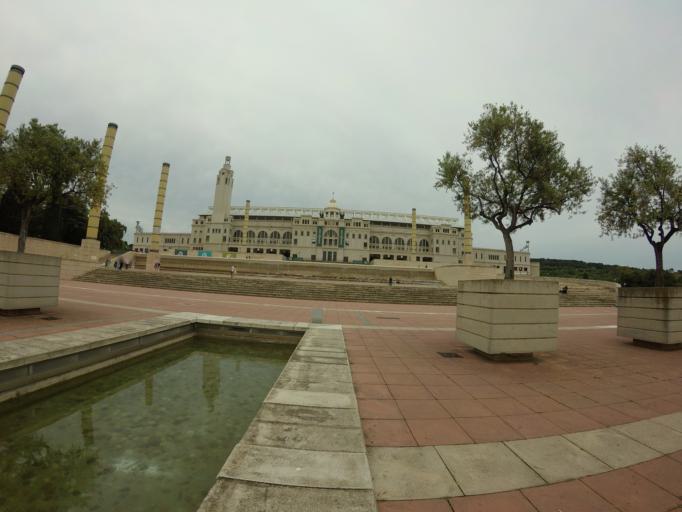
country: ES
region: Catalonia
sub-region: Provincia de Barcelona
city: Sants-Montjuic
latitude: 41.3648
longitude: 2.1530
